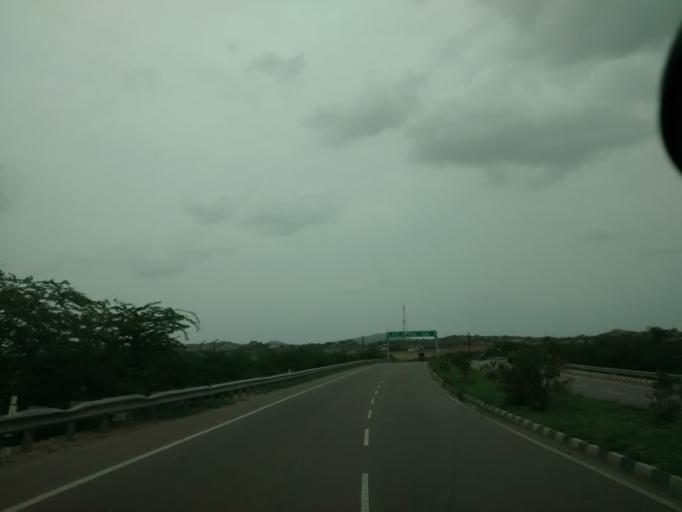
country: IN
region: Andhra Pradesh
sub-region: Kurnool
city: Ramapuram
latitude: 15.1874
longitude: 77.6906
